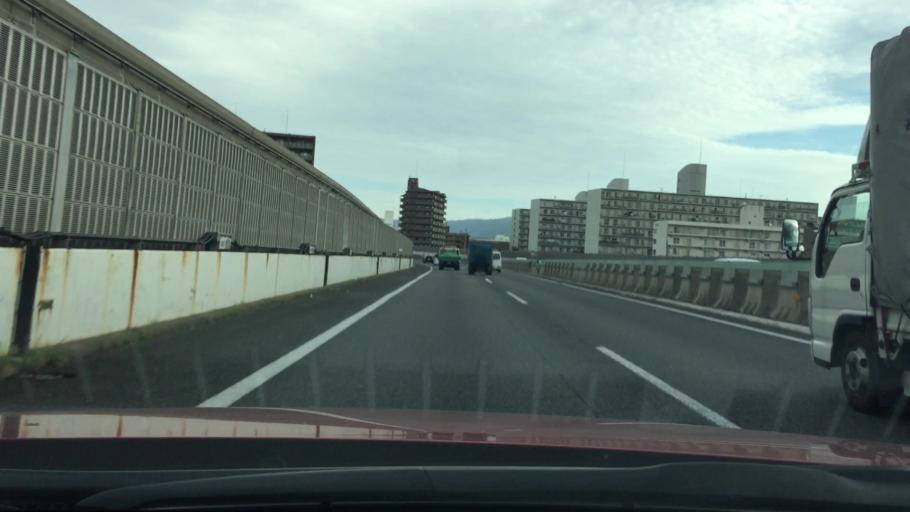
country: JP
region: Osaka
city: Ibaraki
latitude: 34.7971
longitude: 135.5666
